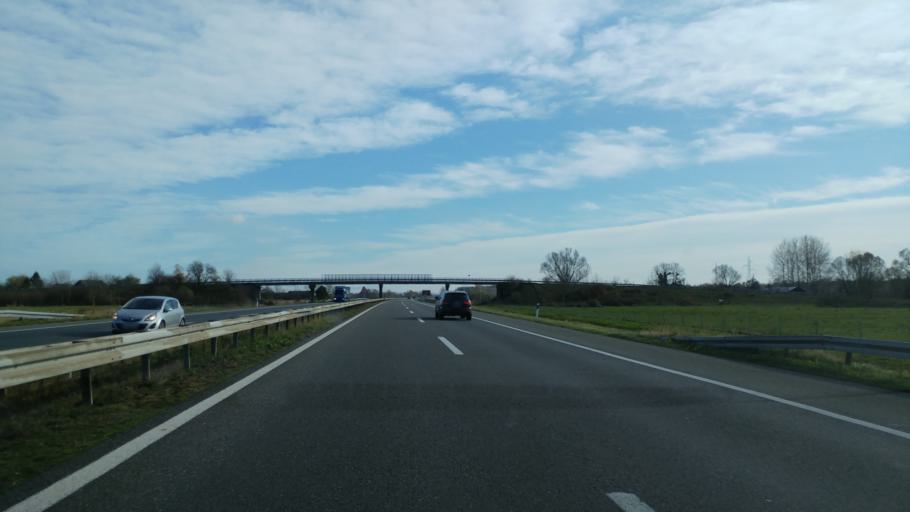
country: HR
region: Sisacko-Moslavacka
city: Repusnica
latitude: 45.4813
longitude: 16.7174
